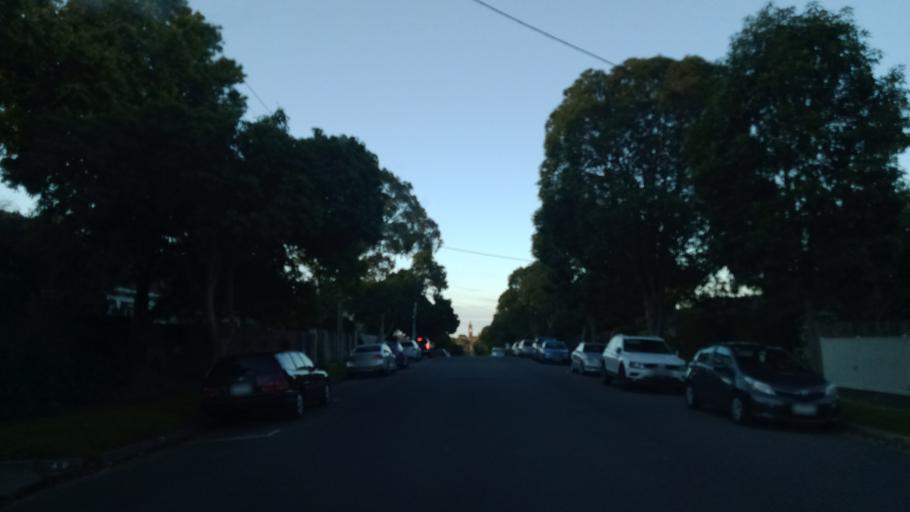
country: AU
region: Victoria
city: Glenferrie
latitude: -37.8331
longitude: 145.0411
